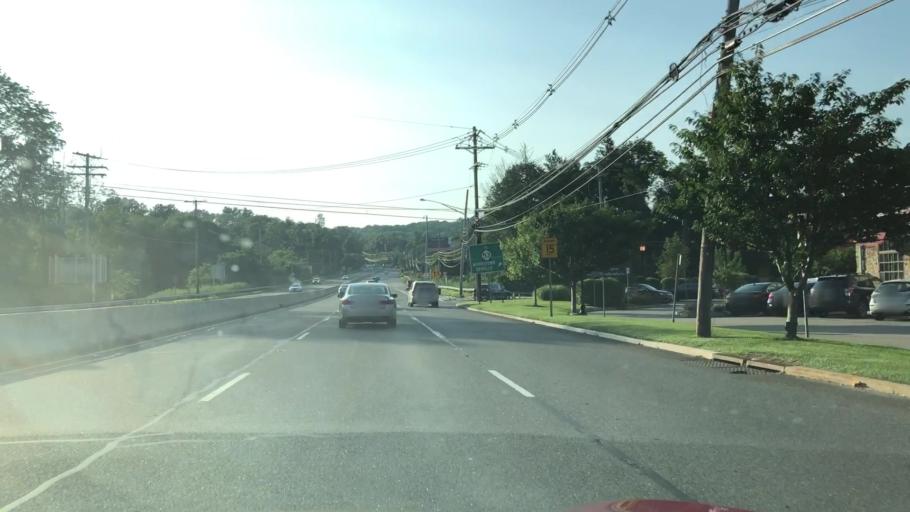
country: US
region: New Jersey
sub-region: Morris County
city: Morris Plains
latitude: 40.8504
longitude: -74.4726
